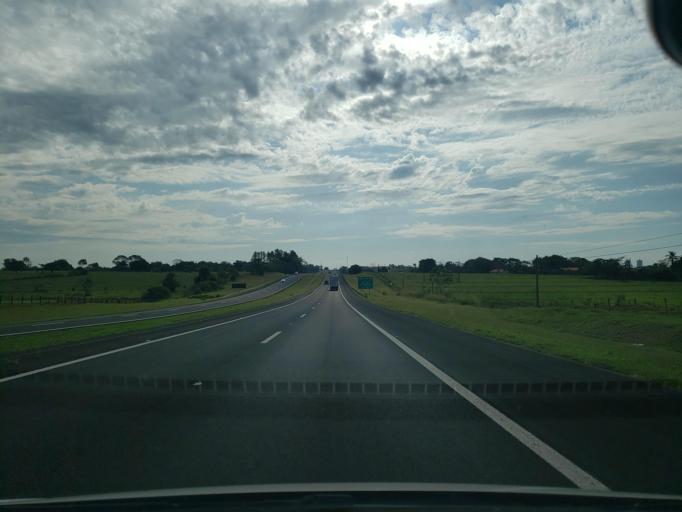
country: BR
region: Sao Paulo
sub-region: Birigui
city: Birigui
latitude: -21.3346
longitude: -50.3304
